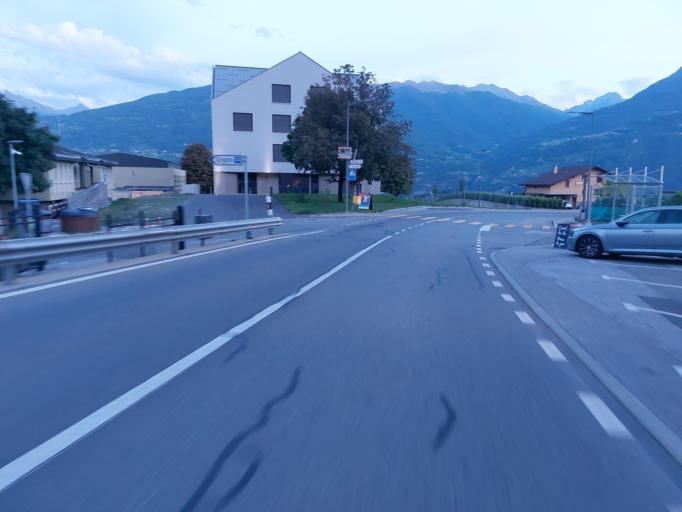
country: CH
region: Valais
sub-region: Conthey District
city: Conthey
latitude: 46.2351
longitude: 7.3049
